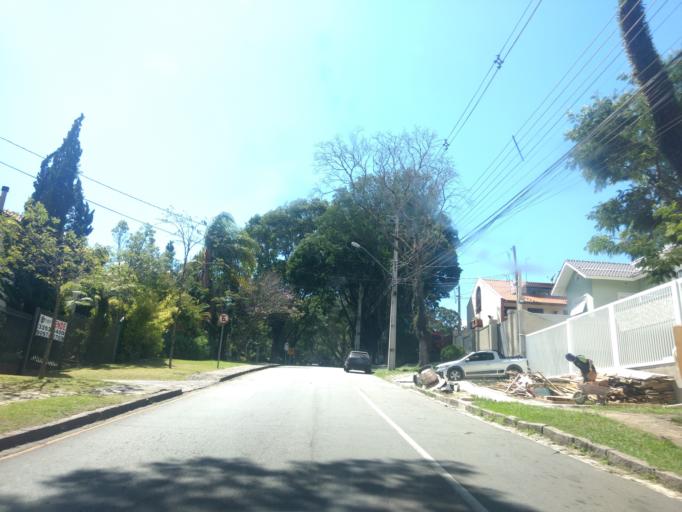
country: BR
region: Parana
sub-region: Curitiba
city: Curitiba
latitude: -25.4107
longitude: -49.2347
